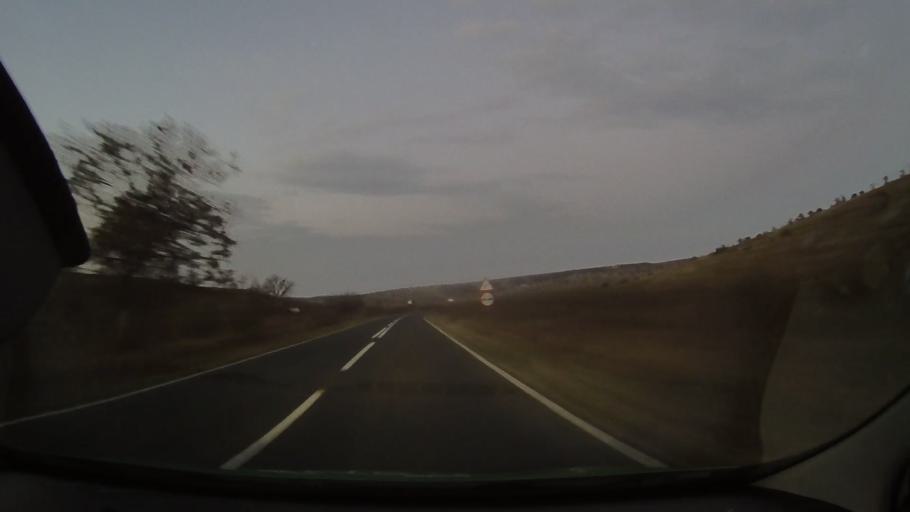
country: RO
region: Constanta
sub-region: Comuna Ion Corvin
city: Ion Corvin
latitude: 44.1074
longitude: 27.7564
